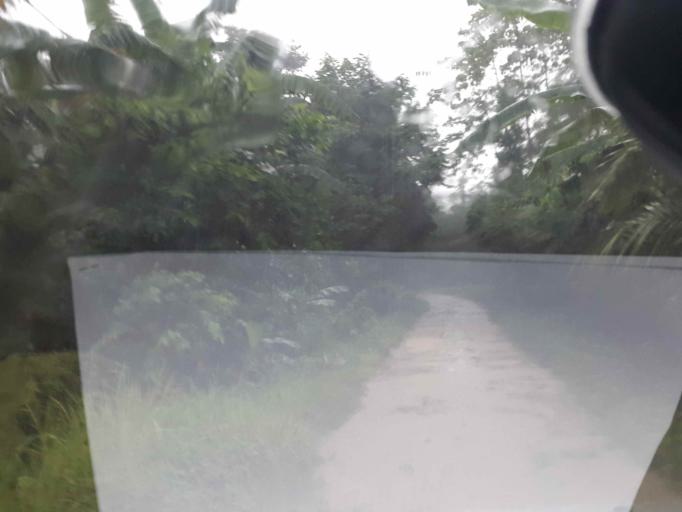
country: ID
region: Lampung
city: Kedaton
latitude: -5.3922
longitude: 105.3368
